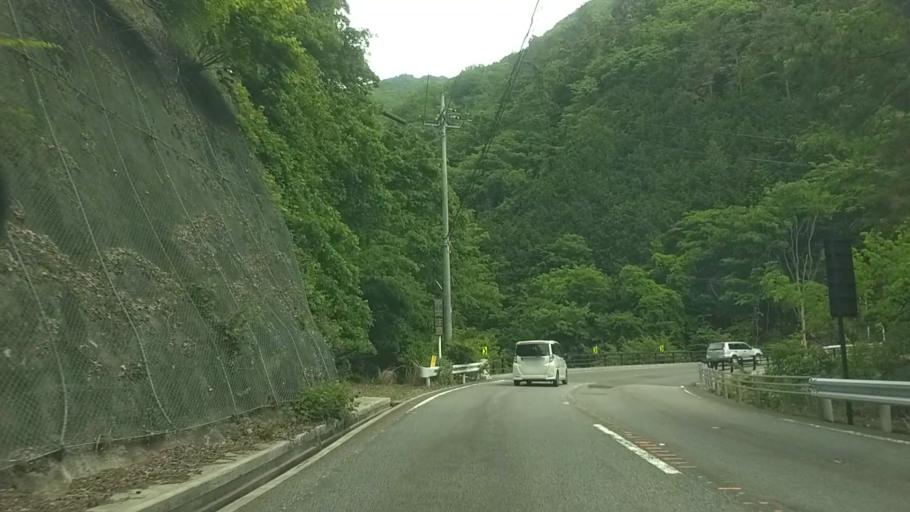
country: JP
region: Yamanashi
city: Fujikawaguchiko
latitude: 35.5216
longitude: 138.6228
